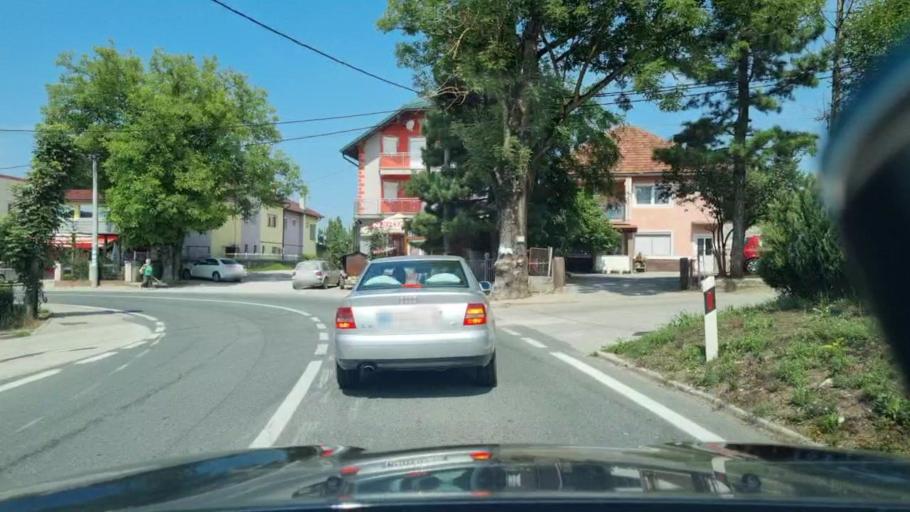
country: BA
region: Federation of Bosnia and Herzegovina
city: Izacic
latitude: 44.8789
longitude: 15.7774
